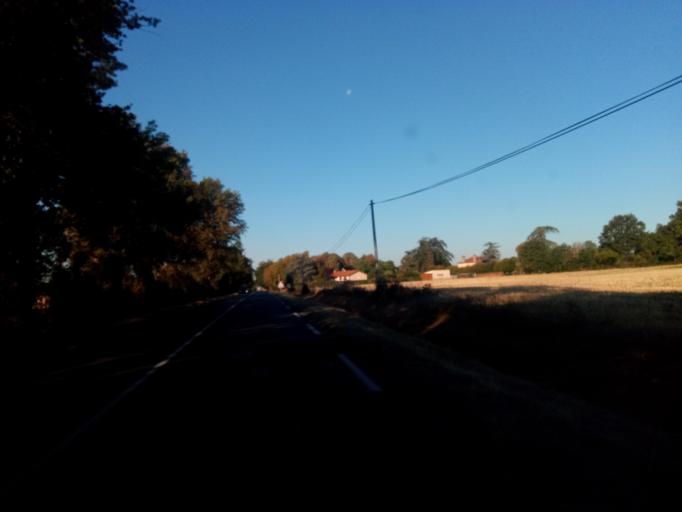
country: FR
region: Poitou-Charentes
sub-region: Departement de la Vienne
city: Lussac-les-Chateaux
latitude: 46.4076
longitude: 0.7979
